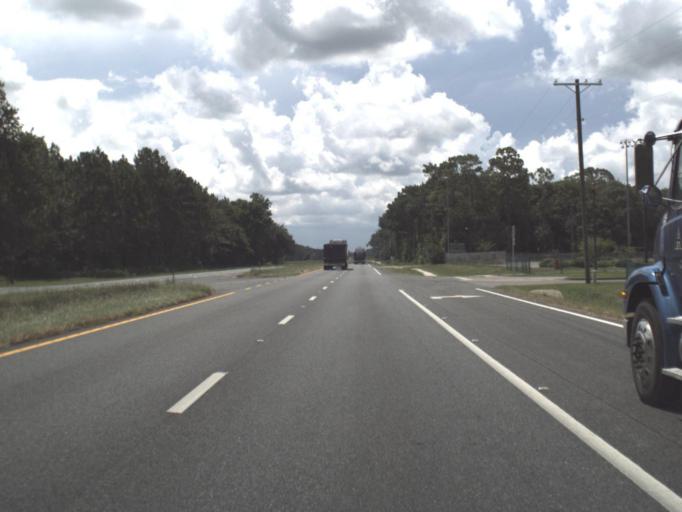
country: US
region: Florida
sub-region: Taylor County
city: Perry
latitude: 30.1383
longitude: -83.6054
